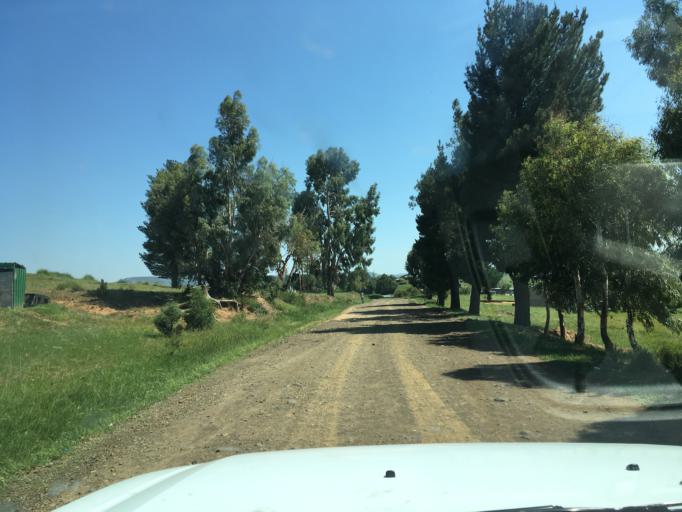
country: LS
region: Butha-Buthe
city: Butha-Buthe
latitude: -28.7255
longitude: 28.3597
